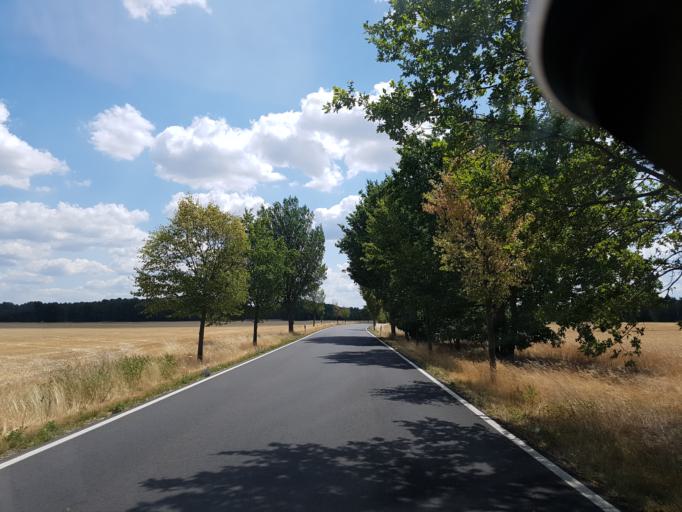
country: DE
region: Brandenburg
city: Cottbus
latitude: 51.7148
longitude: 14.4204
